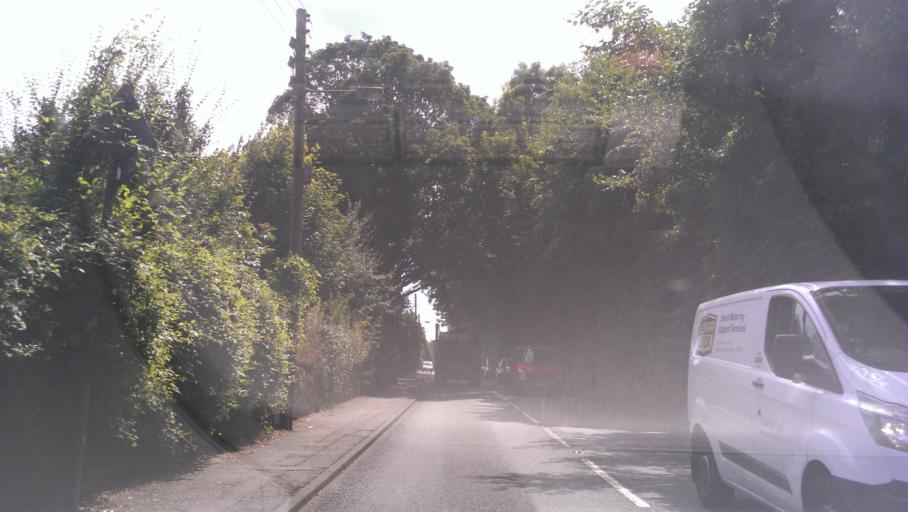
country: GB
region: England
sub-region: Kent
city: Faversham
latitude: 51.3078
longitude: 0.8889
